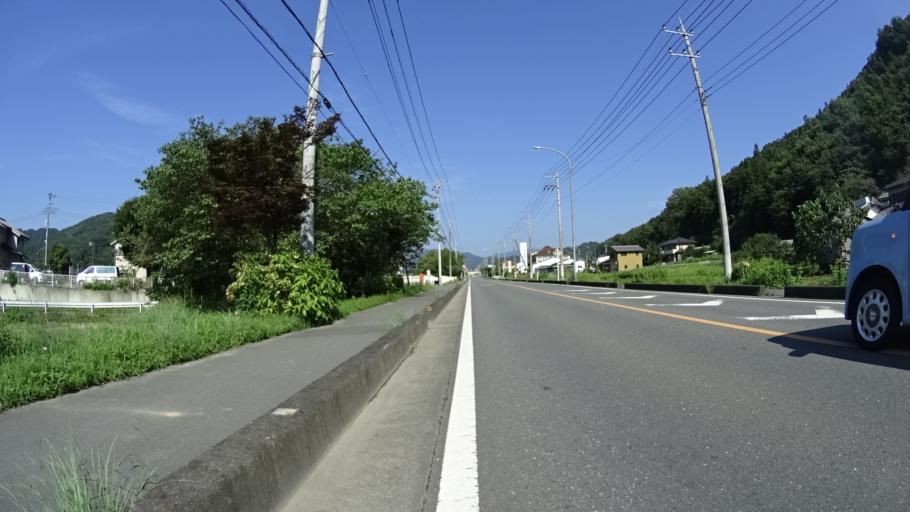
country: JP
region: Saitama
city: Chichibu
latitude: 36.0153
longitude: 139.0193
